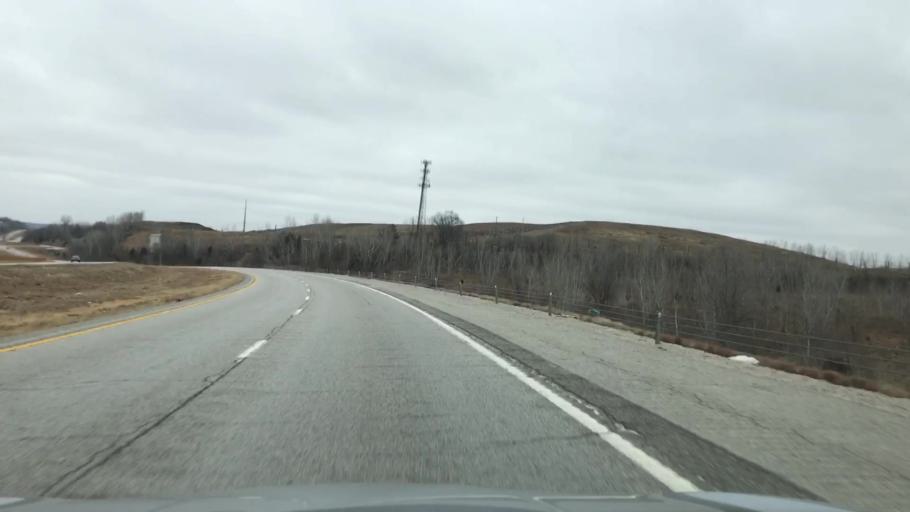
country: US
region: Missouri
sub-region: Jackson County
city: East Independence
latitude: 39.1321
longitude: -94.3836
